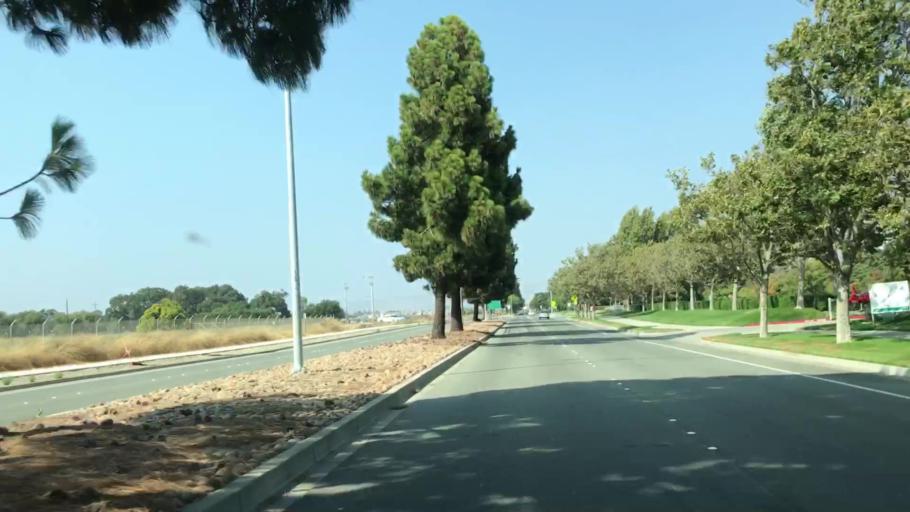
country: US
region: California
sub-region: Alameda County
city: Newark
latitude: 37.5535
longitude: -122.0684
